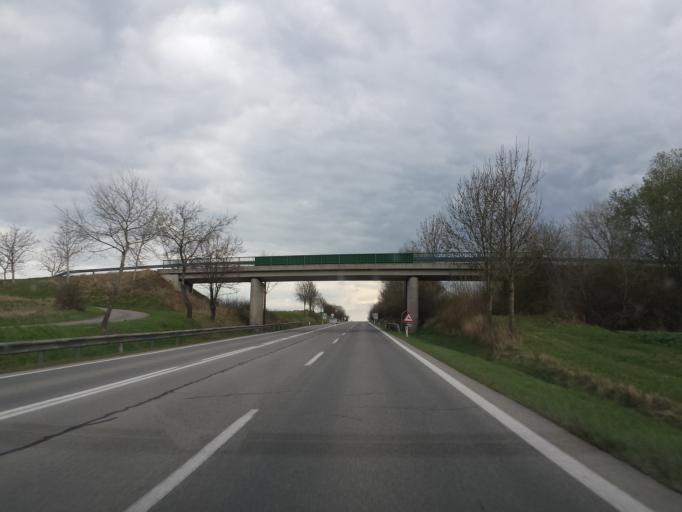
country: AT
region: Lower Austria
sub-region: Politischer Bezirk Krems
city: Lengenfeld
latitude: 48.4638
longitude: 15.5886
